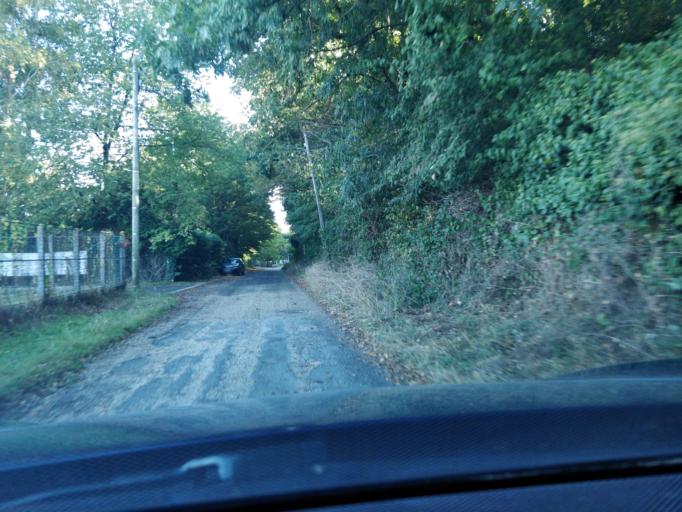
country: FR
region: Ile-de-France
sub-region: Departement de l'Essonne
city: Forges-les-Bains
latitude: 48.6246
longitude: 2.0950
